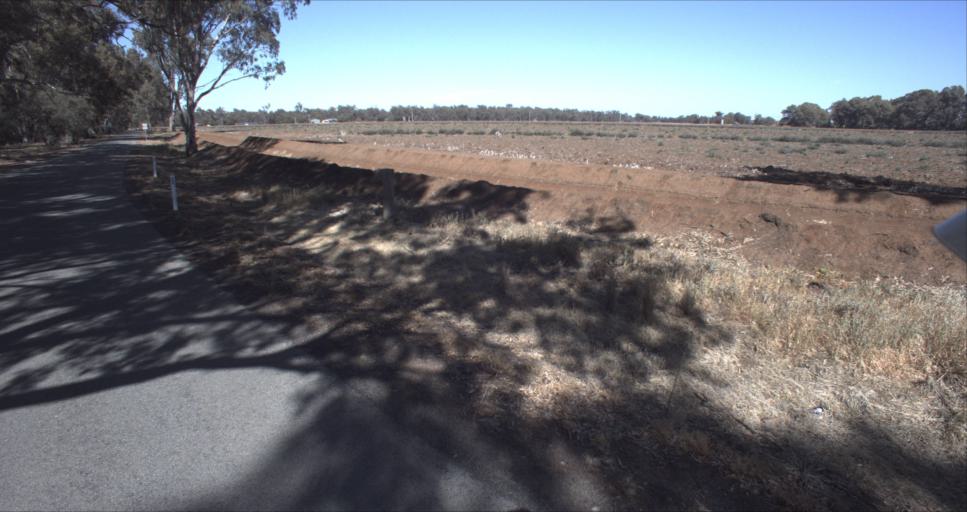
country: AU
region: New South Wales
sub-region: Leeton
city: Leeton
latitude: -34.6073
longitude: 146.2629
